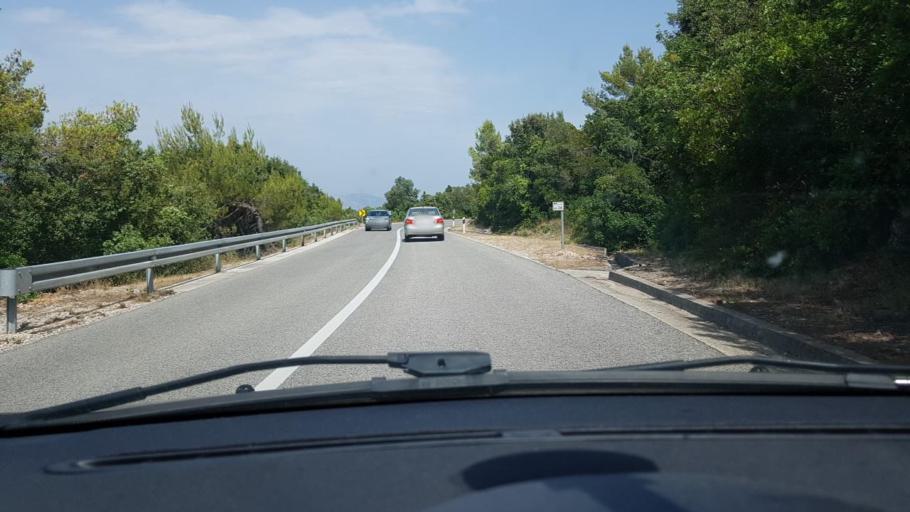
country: HR
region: Dubrovacko-Neretvanska
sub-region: Grad Korcula
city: Zrnovo
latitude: 42.9399
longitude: 17.0653
